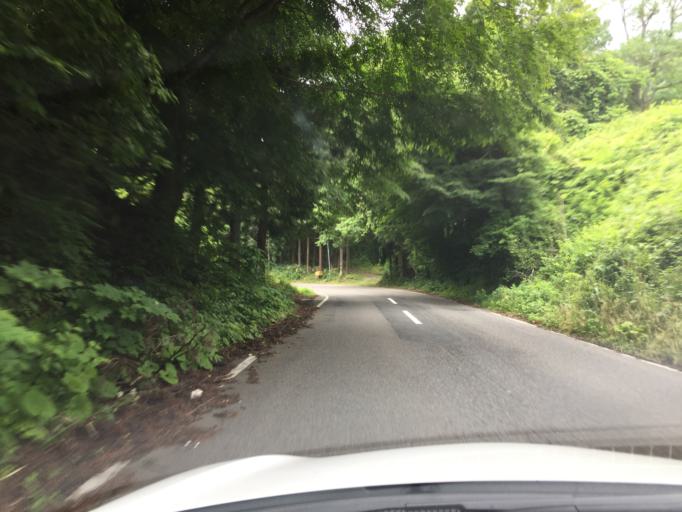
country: JP
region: Fukushima
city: Miharu
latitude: 37.3046
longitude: 140.5436
